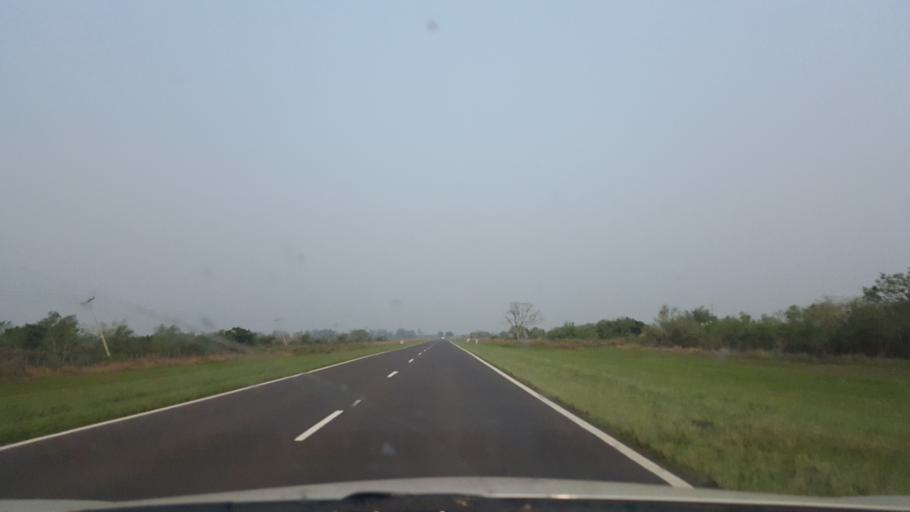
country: AR
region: Corrientes
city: Ita Ibate
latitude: -27.4623
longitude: -57.3142
